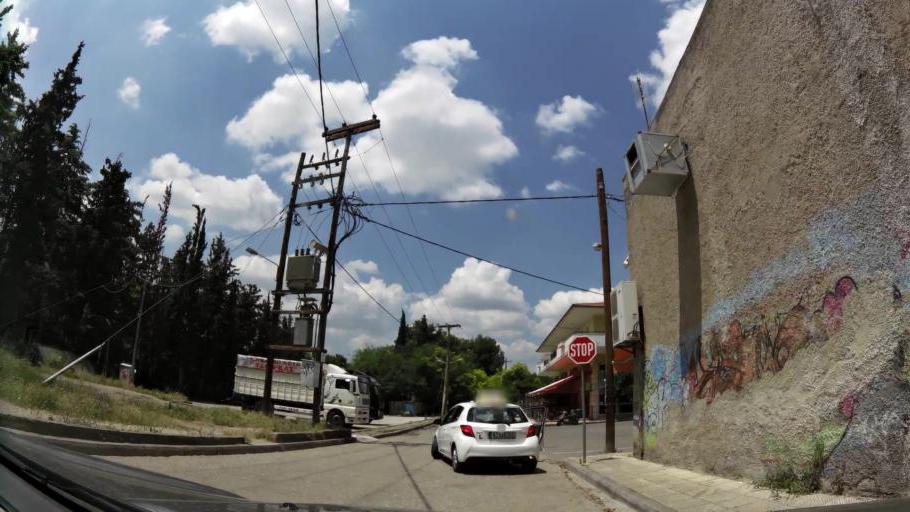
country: GR
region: West Macedonia
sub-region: Nomos Kozanis
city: Kozani
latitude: 40.2950
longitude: 21.7948
